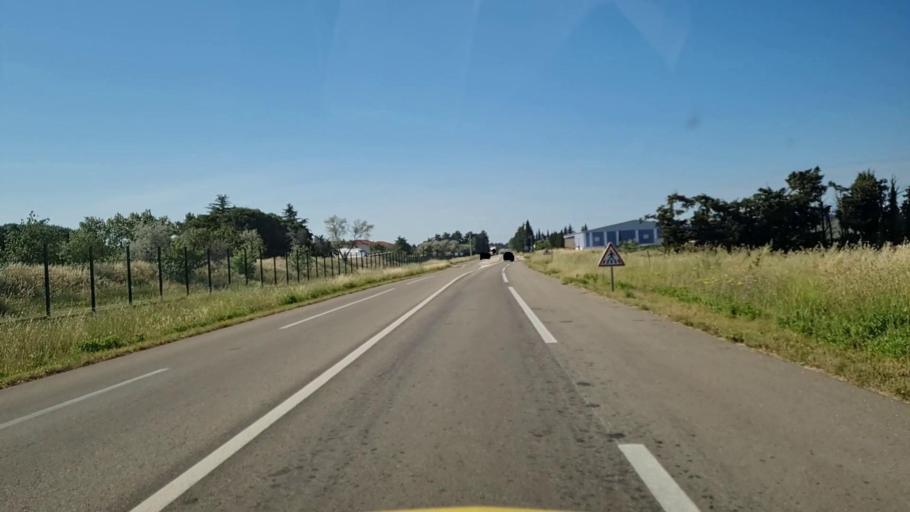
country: FR
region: Languedoc-Roussillon
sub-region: Departement du Gard
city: Garons
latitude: 43.7669
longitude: 4.4055
